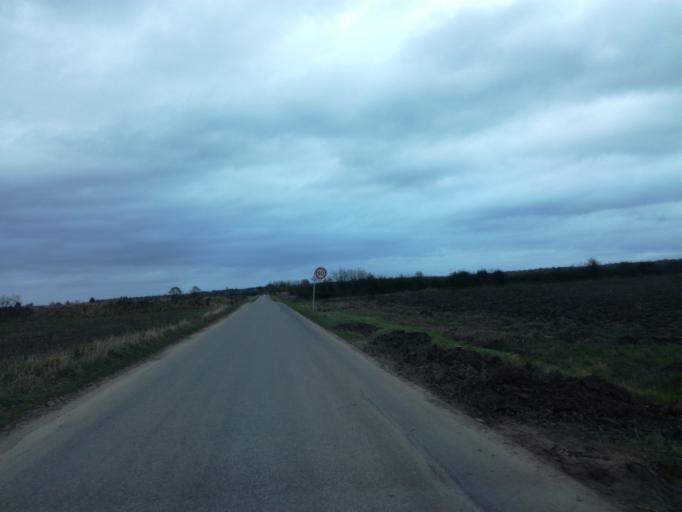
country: DK
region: South Denmark
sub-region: Fredericia Kommune
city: Fredericia
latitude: 55.6128
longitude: 9.7788
